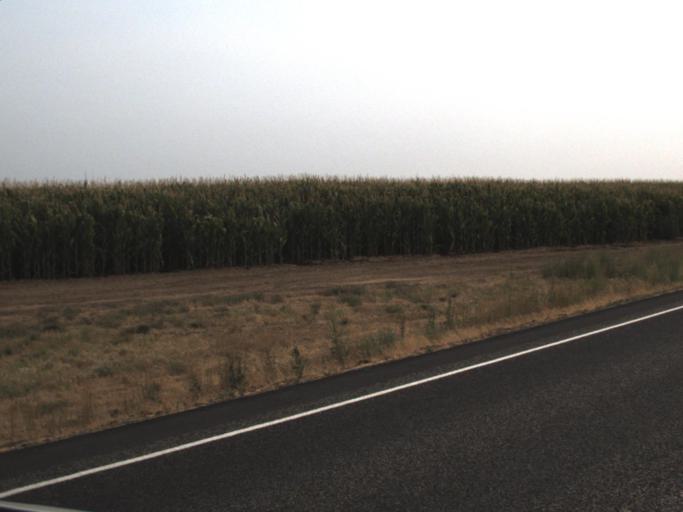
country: US
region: Washington
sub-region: Benton County
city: Benton City
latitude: 46.1070
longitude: -119.6018
